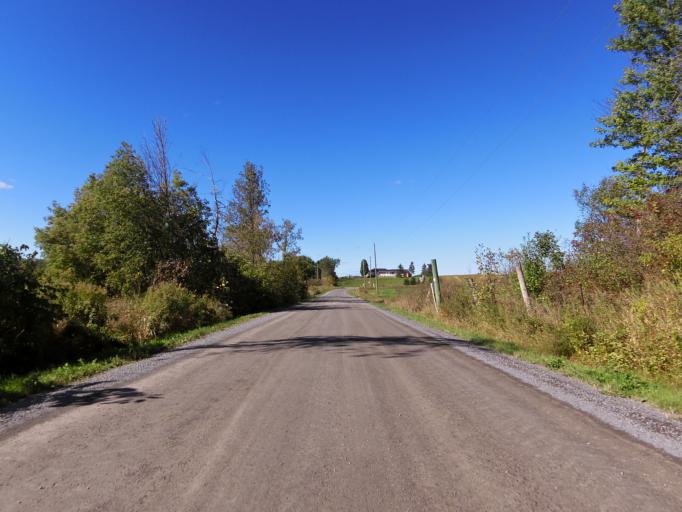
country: CA
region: Ontario
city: Clarence-Rockland
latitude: 45.4083
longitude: -75.3715
